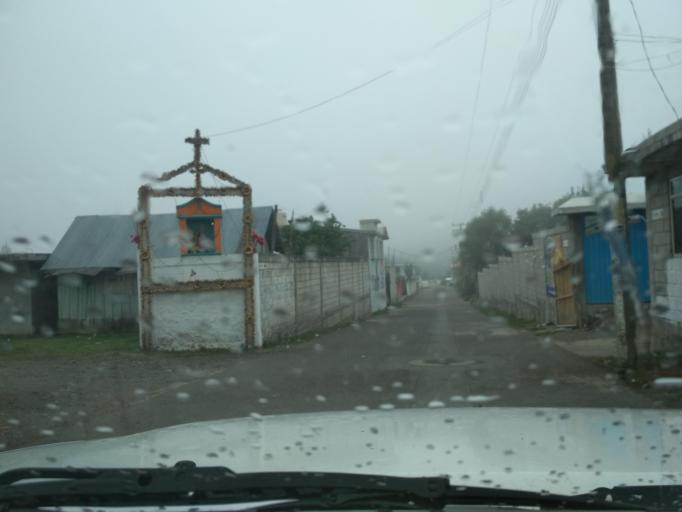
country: MX
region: Veracruz
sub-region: Mariano Escobedo
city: San Isidro el Berro
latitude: 18.9259
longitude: -97.2061
